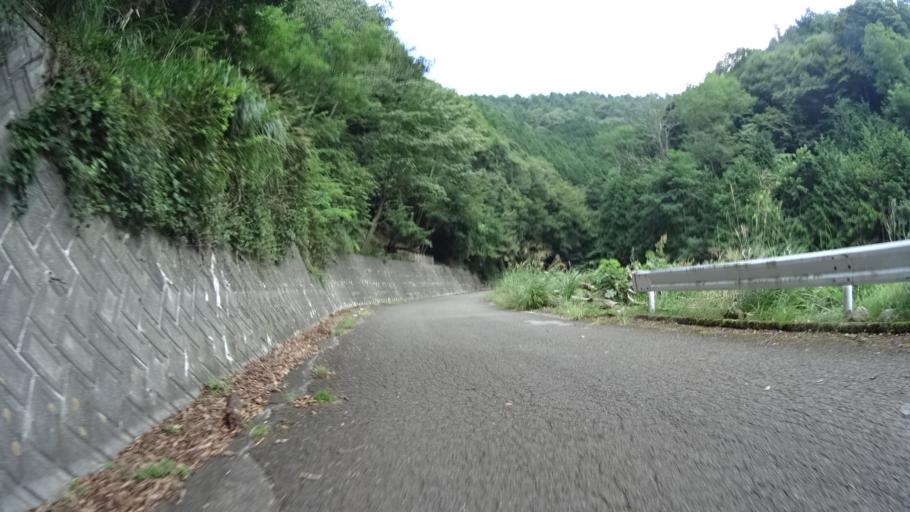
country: JP
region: Yamanashi
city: Enzan
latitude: 35.6217
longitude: 138.7743
